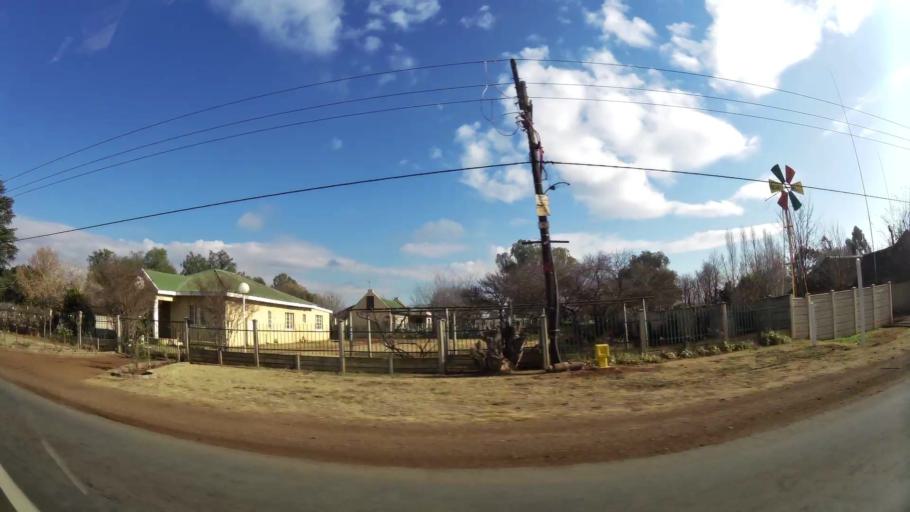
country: ZA
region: Gauteng
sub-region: Sedibeng District Municipality
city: Meyerton
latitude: -26.5202
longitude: 28.0459
